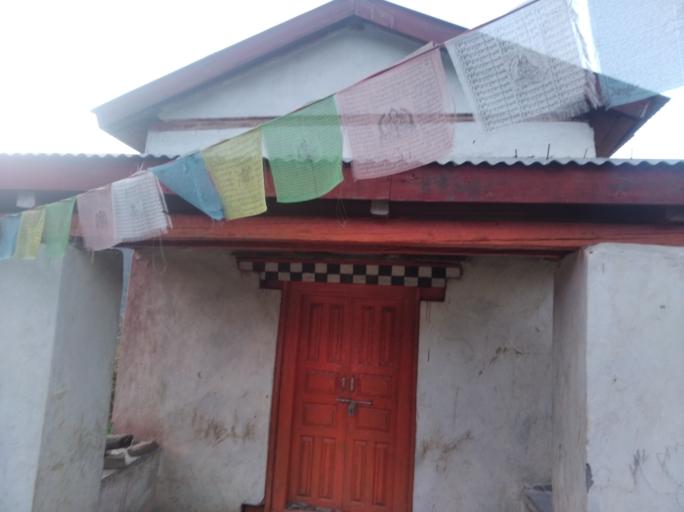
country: NP
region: Western Region
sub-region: Dhawalagiri Zone
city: Jomsom
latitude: 28.8731
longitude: 82.9923
